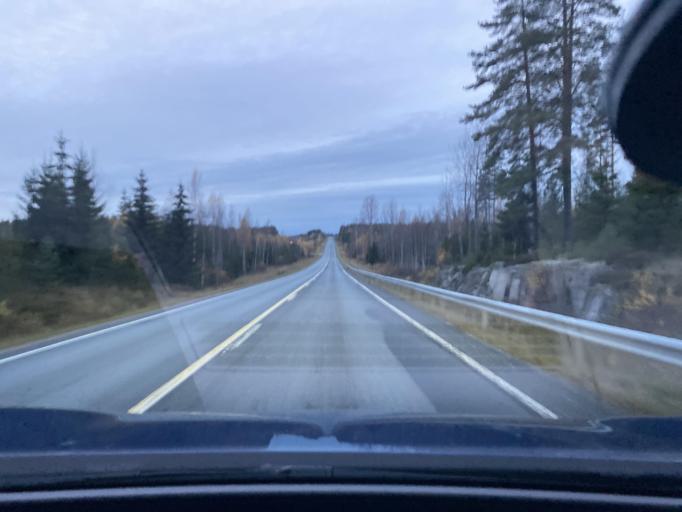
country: FI
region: Varsinais-Suomi
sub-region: Salo
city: Suomusjaervi
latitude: 60.3790
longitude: 23.7371
